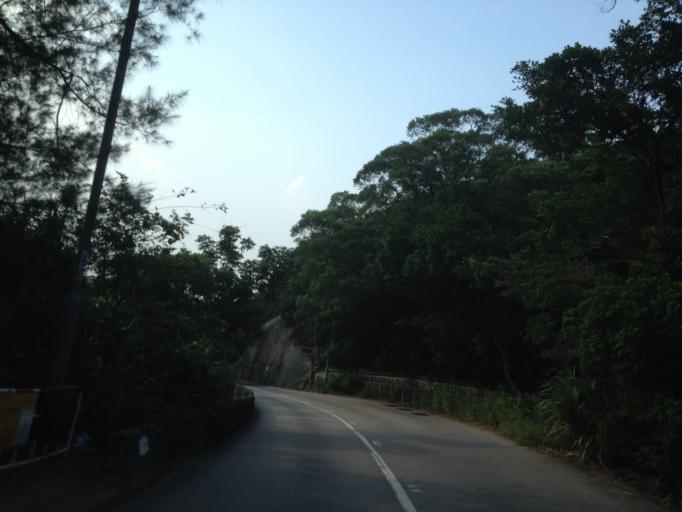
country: HK
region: Wanchai
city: Wan Chai
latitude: 22.2550
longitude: 114.2275
